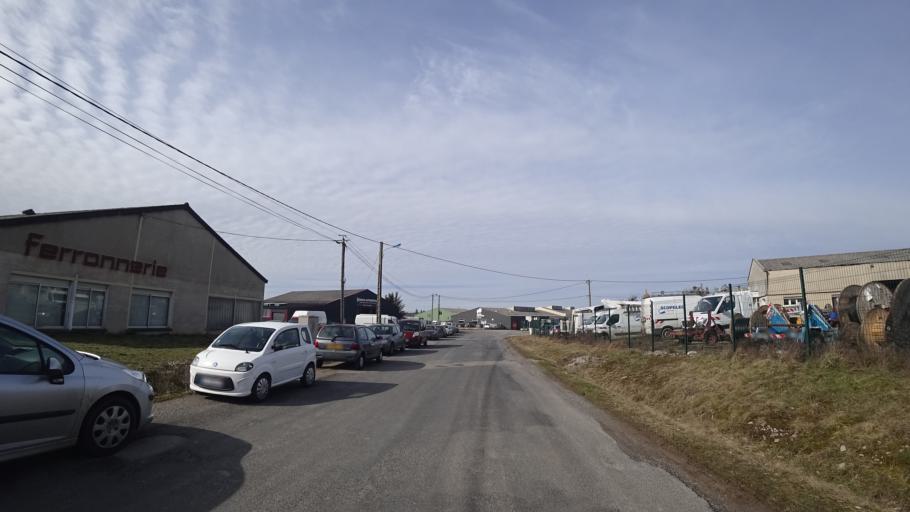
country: FR
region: Midi-Pyrenees
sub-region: Departement de l'Aveyron
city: Olemps
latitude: 44.3764
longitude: 2.5498
